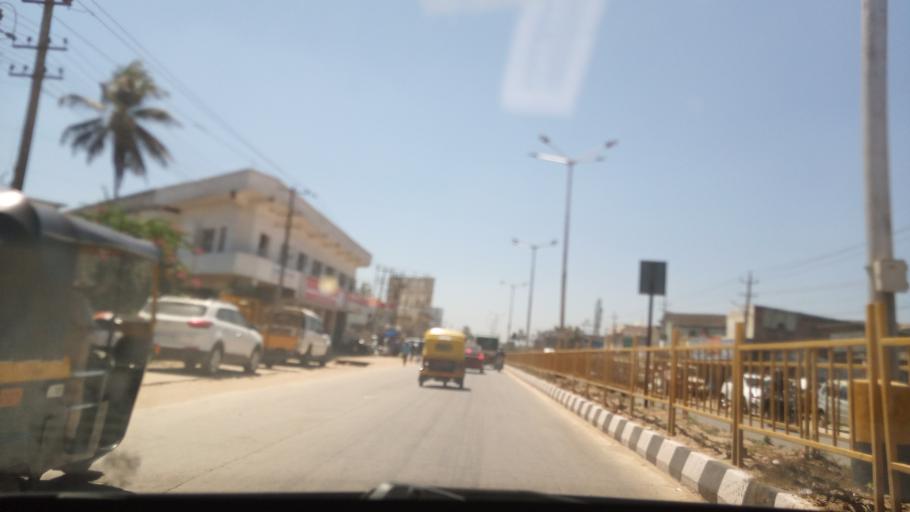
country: IN
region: Karnataka
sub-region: Hassan
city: Hassan
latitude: 12.9970
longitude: 76.0899
